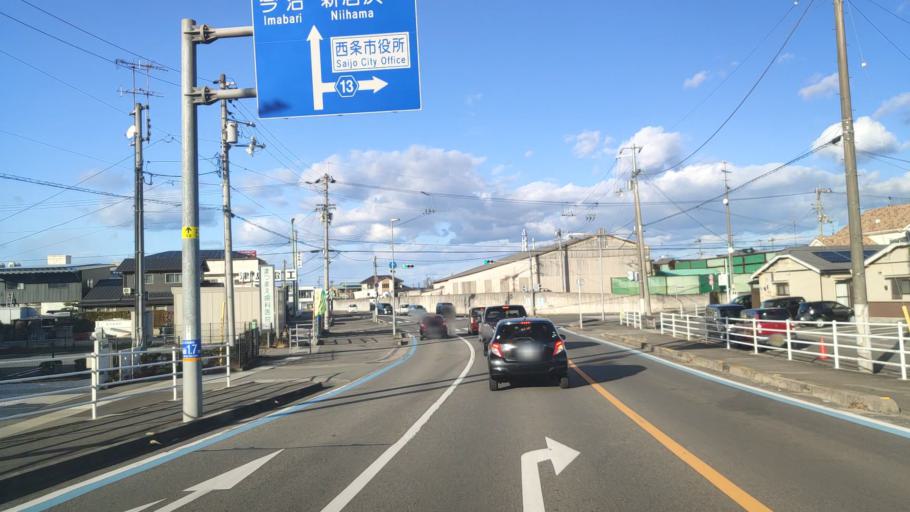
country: JP
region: Ehime
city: Saijo
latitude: 33.9147
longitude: 133.1622
